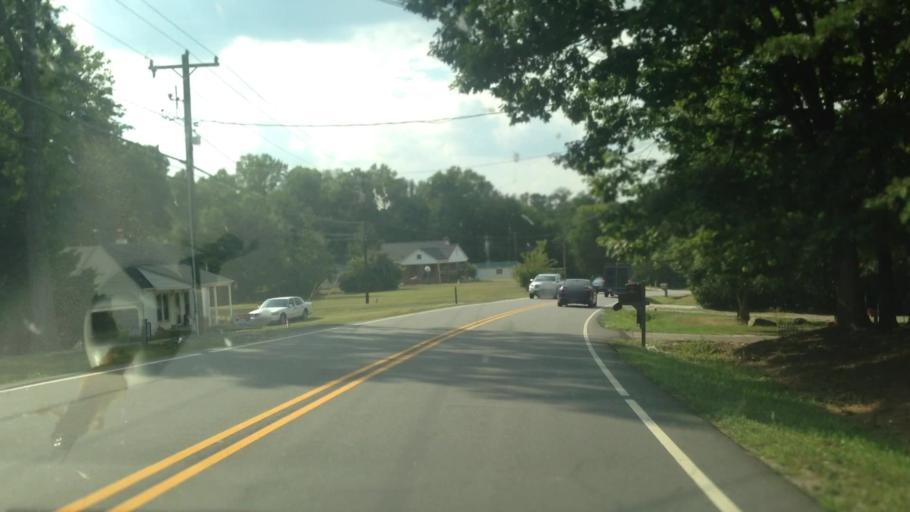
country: US
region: North Carolina
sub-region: Forsyth County
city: Kernersville
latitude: 36.1239
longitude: -80.1113
